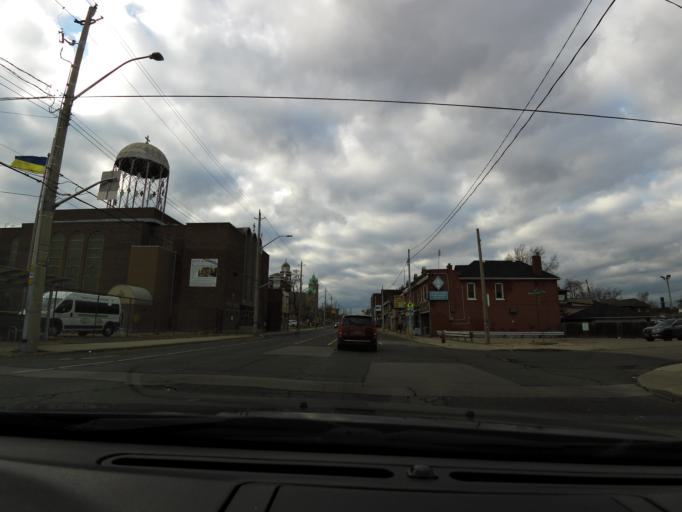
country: CA
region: Ontario
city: Hamilton
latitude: 43.2558
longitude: -79.8331
